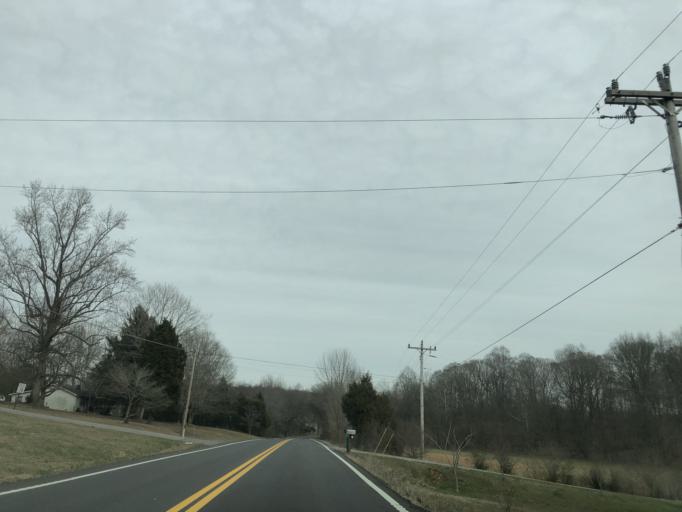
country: US
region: Tennessee
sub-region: Robertson County
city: Greenbrier
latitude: 36.4743
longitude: -86.7481
